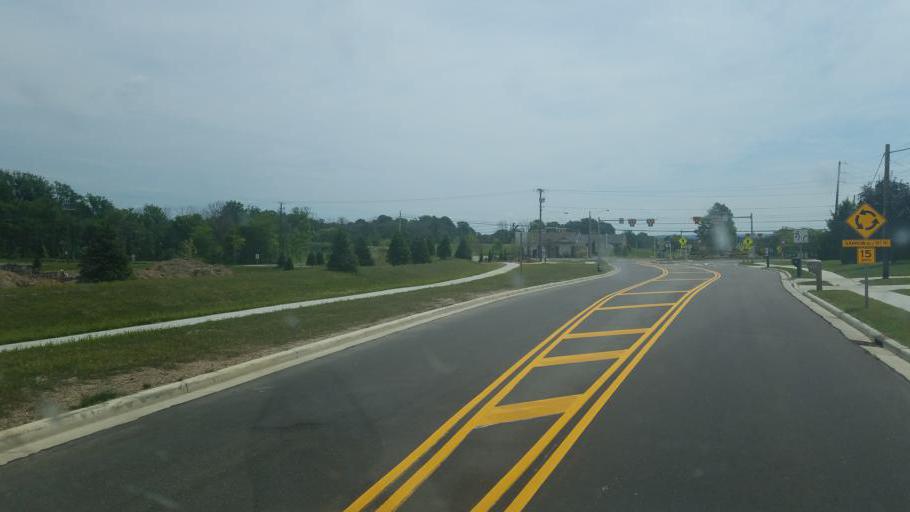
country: US
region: Ohio
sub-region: Summit County
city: Twinsburg
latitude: 41.3409
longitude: -81.4416
